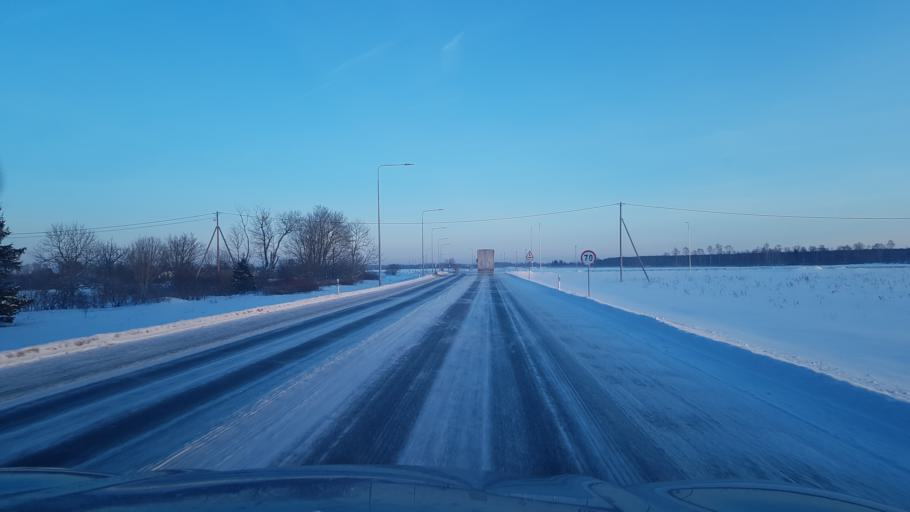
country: EE
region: Ida-Virumaa
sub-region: Narva-Joesuu linn
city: Narva-Joesuu
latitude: 59.3919
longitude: 28.0906
